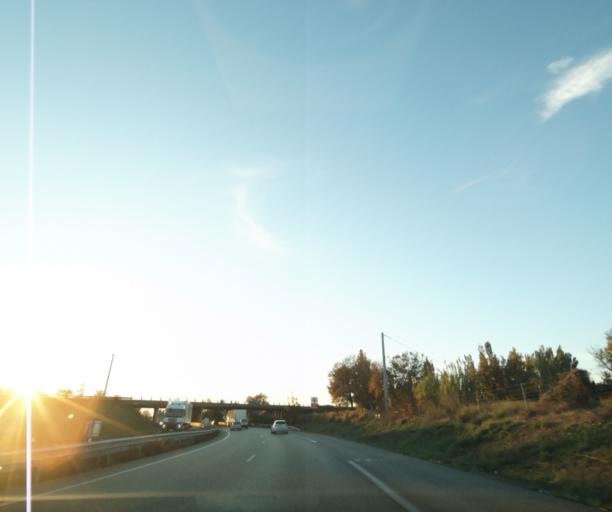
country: FR
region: Provence-Alpes-Cote d'Azur
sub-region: Departement des Bouches-du-Rhone
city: Pelissanne
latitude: 43.6285
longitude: 5.1287
